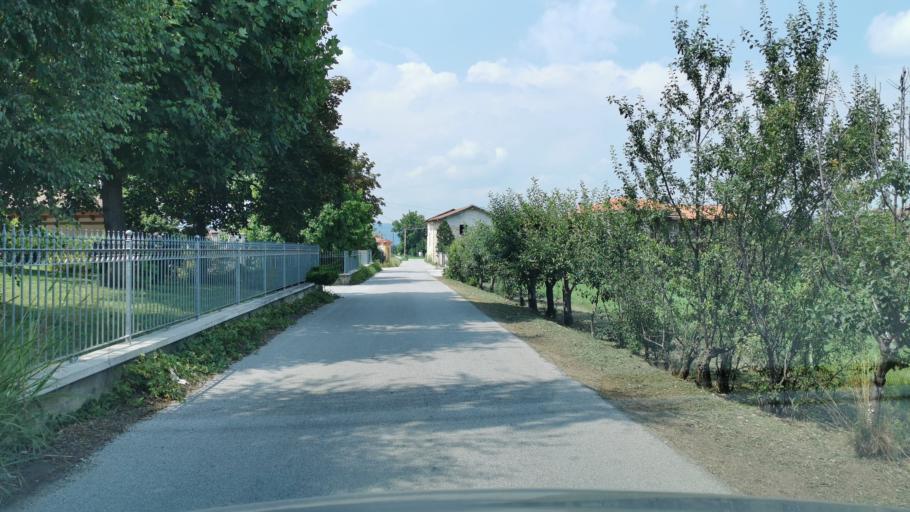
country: IT
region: Piedmont
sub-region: Provincia di Cuneo
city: Caraglio
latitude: 44.4253
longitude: 7.4526
